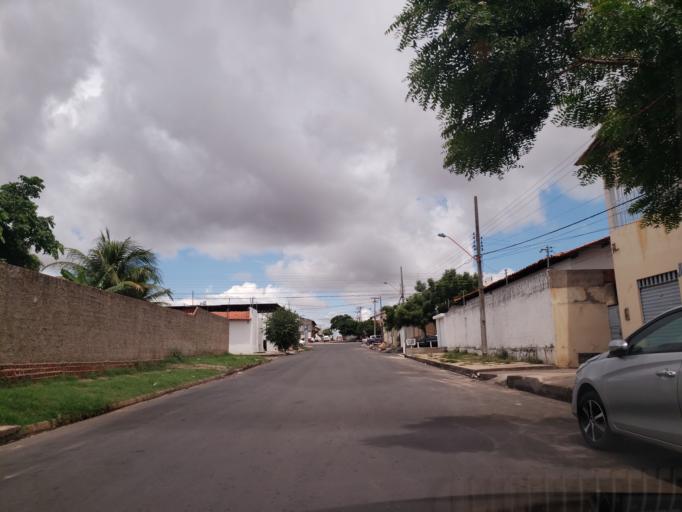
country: BR
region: Piaui
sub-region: Teresina
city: Teresina
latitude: -5.1085
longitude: -42.8092
